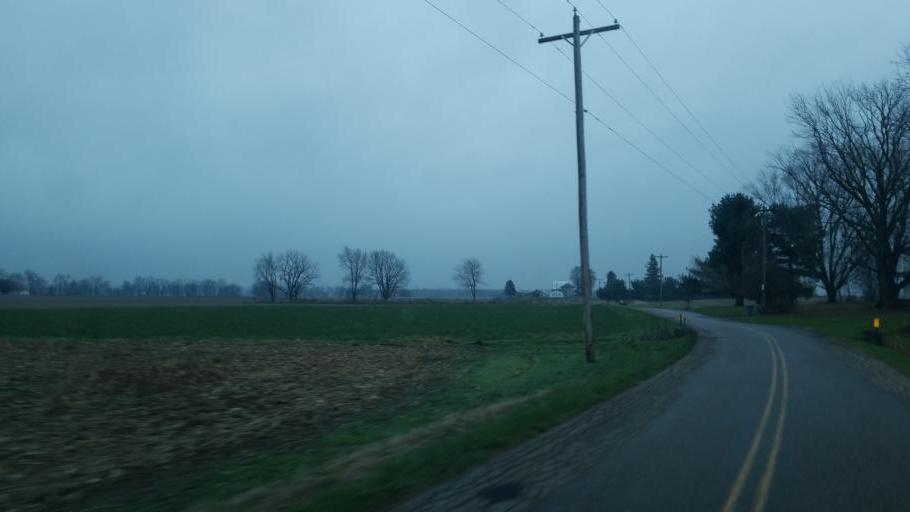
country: US
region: Ohio
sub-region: Knox County
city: Fredericktown
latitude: 40.4491
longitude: -82.5724
